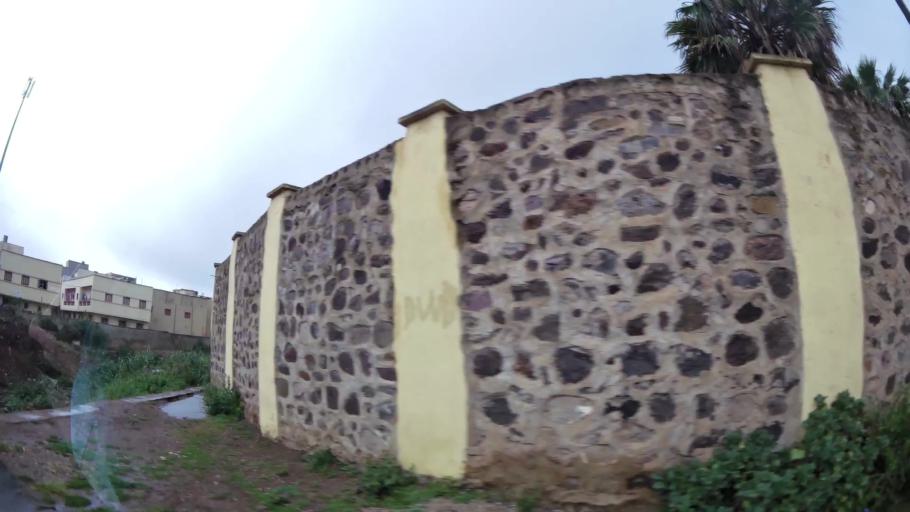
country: MA
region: Oriental
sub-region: Nador
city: Nador
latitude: 35.1586
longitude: -2.9526
